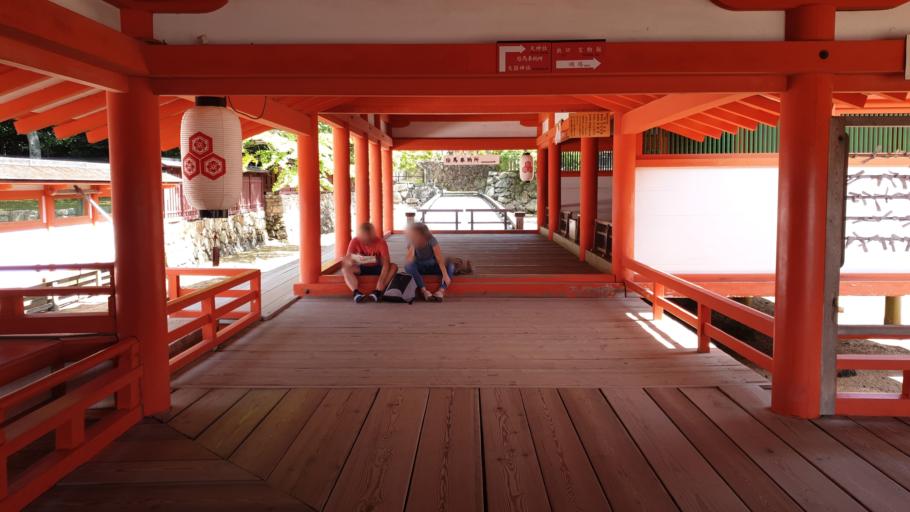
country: JP
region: Hiroshima
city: Miyajima
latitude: 34.2958
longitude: 132.3197
